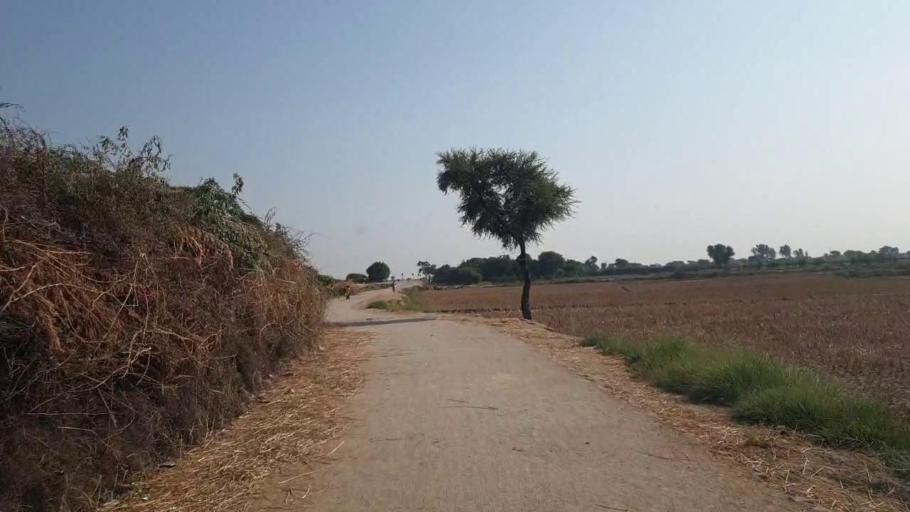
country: PK
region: Sindh
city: Matli
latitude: 24.9657
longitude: 68.6795
